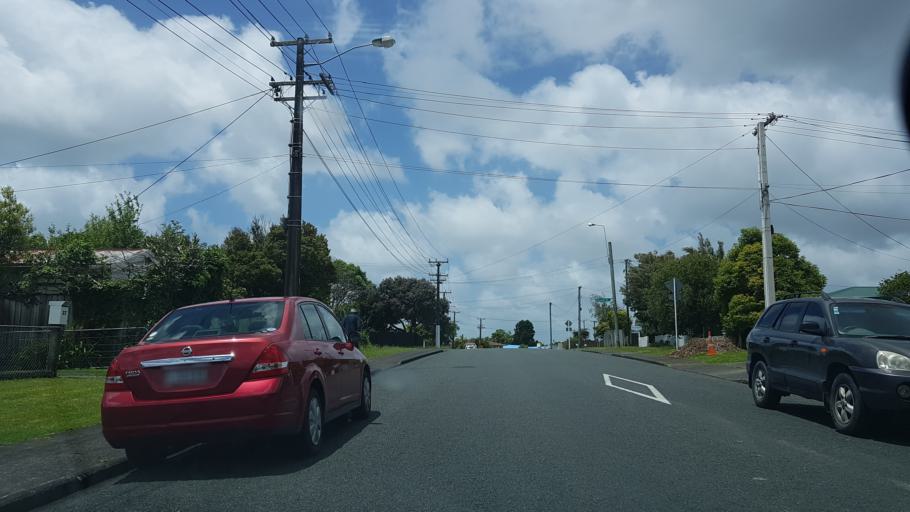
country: NZ
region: Auckland
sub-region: Auckland
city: North Shore
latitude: -36.7942
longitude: 174.6915
